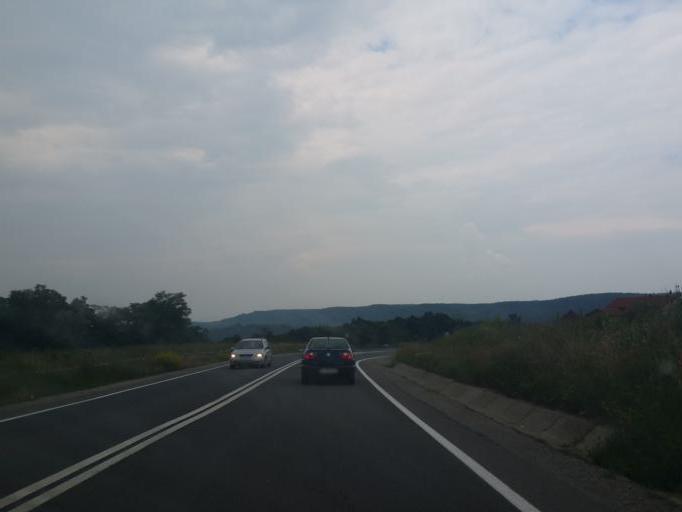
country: RO
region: Cluj
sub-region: Comuna Sanpaul
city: Sanpaul
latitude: 46.9412
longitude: 23.3828
